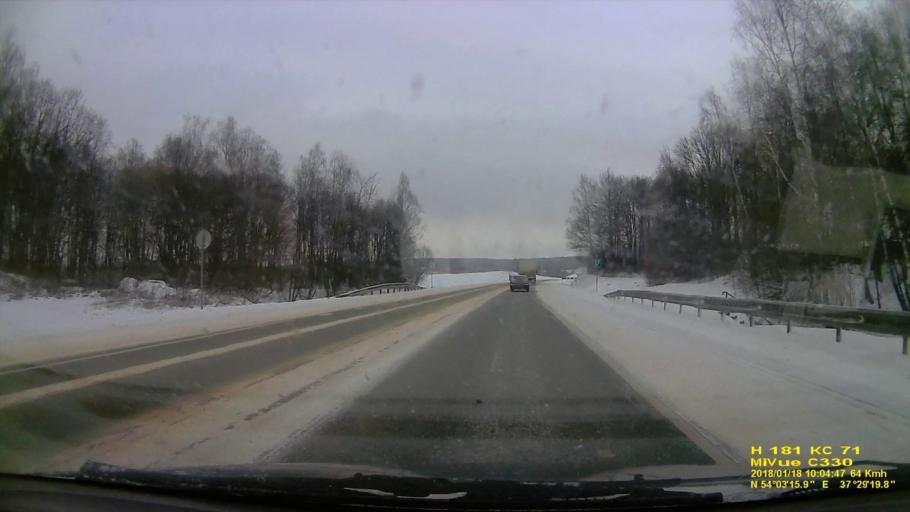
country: RU
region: Tula
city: Pervomayskiy
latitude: 54.0543
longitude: 37.4889
